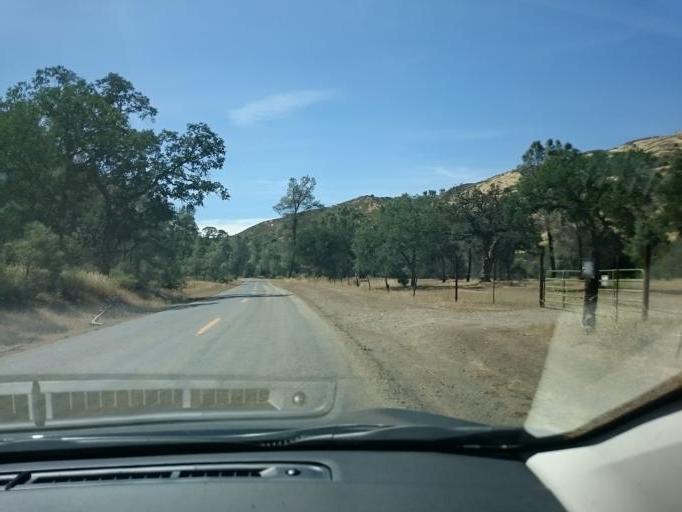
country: US
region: California
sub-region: Stanislaus County
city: Patterson
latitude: 37.4222
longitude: -121.3630
